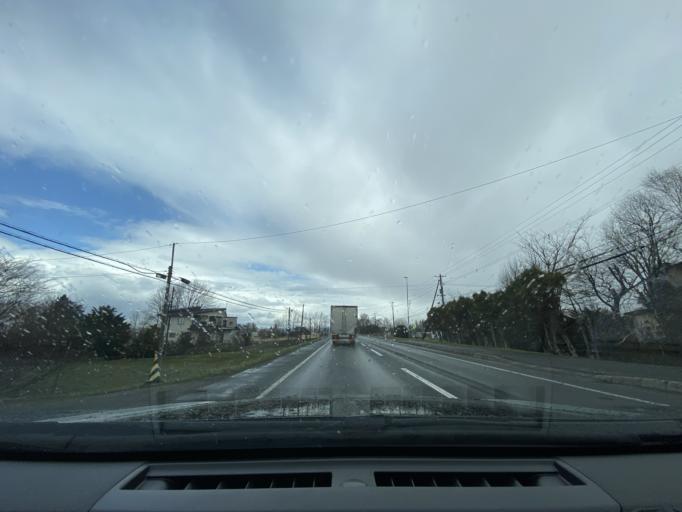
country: JP
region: Hokkaido
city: Fukagawa
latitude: 43.6873
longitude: 142.0500
